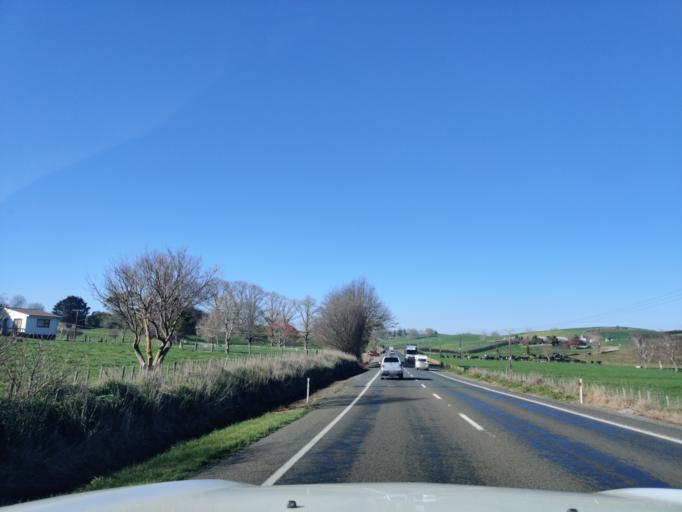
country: NZ
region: Waikato
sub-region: Matamata-Piako District
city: Matamata
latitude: -38.0024
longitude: 175.7676
